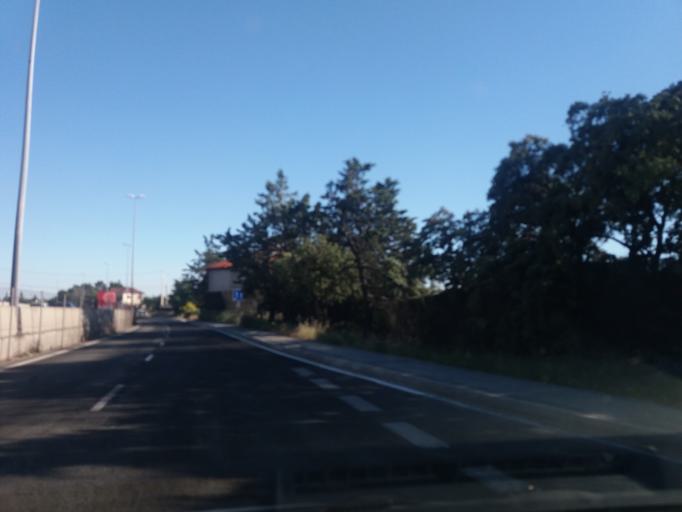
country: ES
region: Madrid
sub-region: Provincia de Madrid
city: Torrelodones
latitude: 40.5889
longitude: -3.9544
